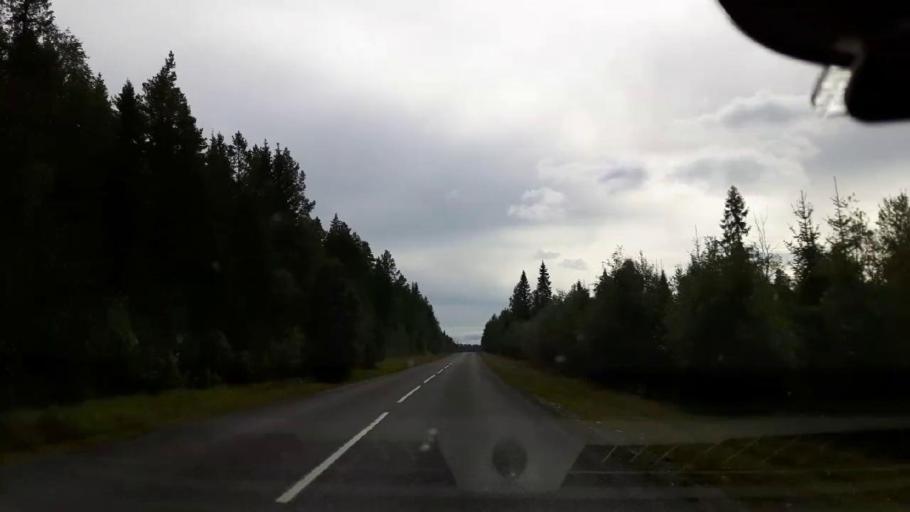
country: SE
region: Jaemtland
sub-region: Ragunda Kommun
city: Hammarstrand
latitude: 63.0979
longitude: 15.9155
